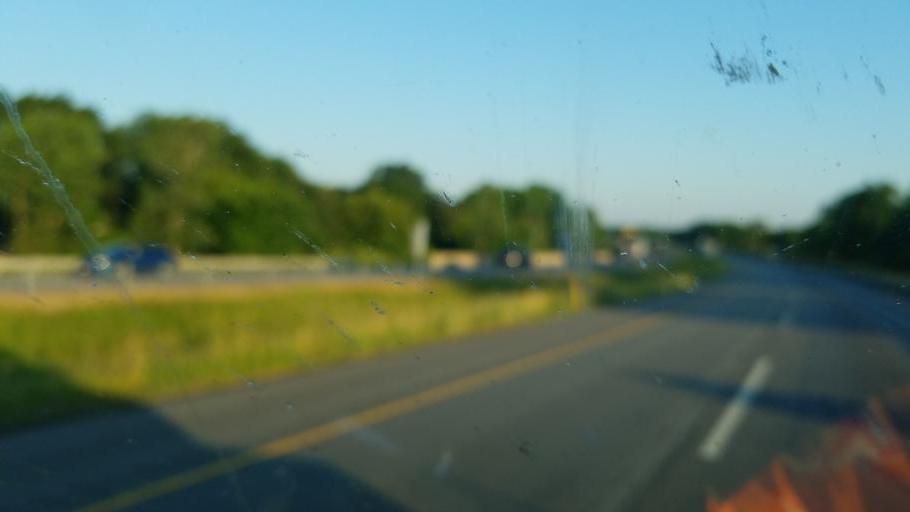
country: US
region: Indiana
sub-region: Porter County
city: Portage
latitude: 41.5782
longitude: -87.1595
